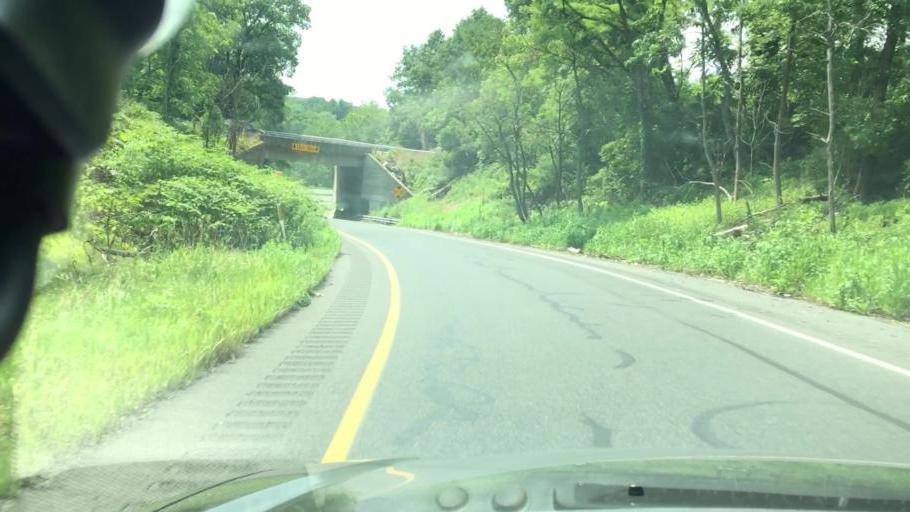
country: US
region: Pennsylvania
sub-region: Monroe County
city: Arlington Heights
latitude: 40.9870
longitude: -75.2309
